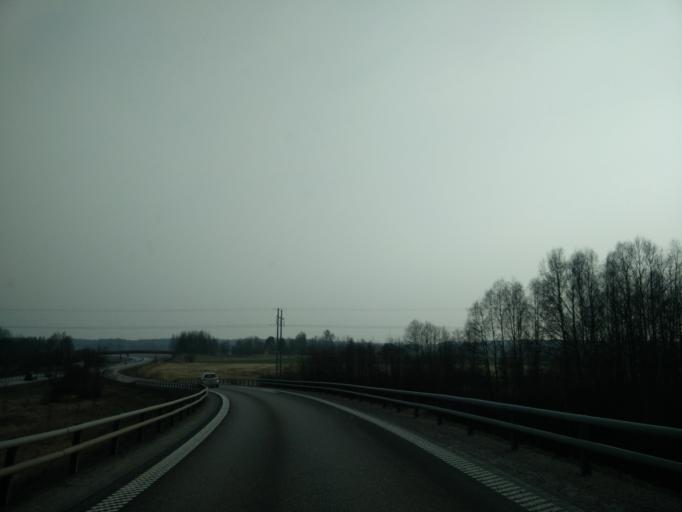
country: SE
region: Vaermland
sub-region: Karlstads Kommun
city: Karlstad
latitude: 59.4265
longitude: 13.4086
